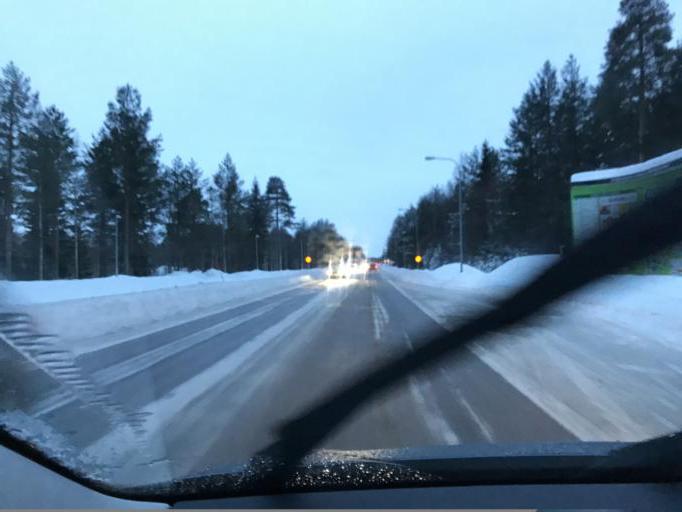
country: SE
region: Norrbotten
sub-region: Lulea Kommun
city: Gammelstad
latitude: 65.6289
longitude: 22.0372
